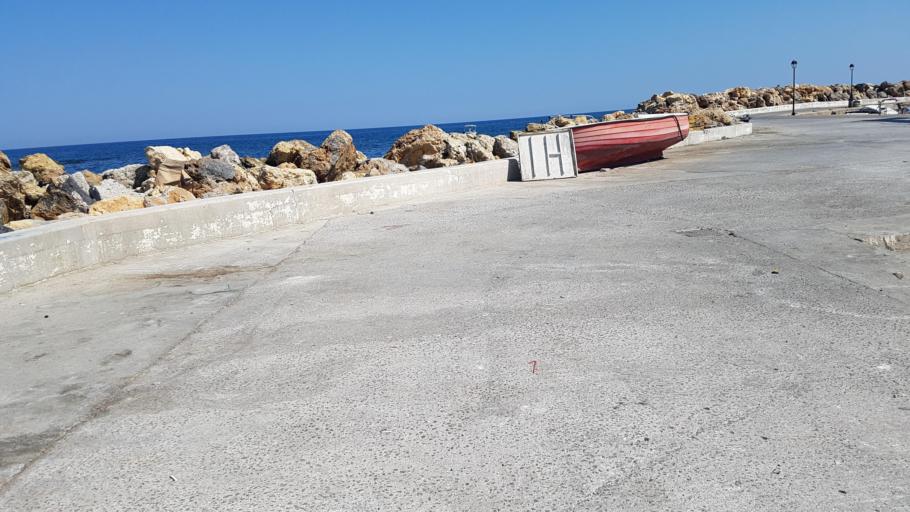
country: GR
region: Crete
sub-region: Nomos Chanias
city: Chania
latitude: 35.5158
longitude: 24.0076
